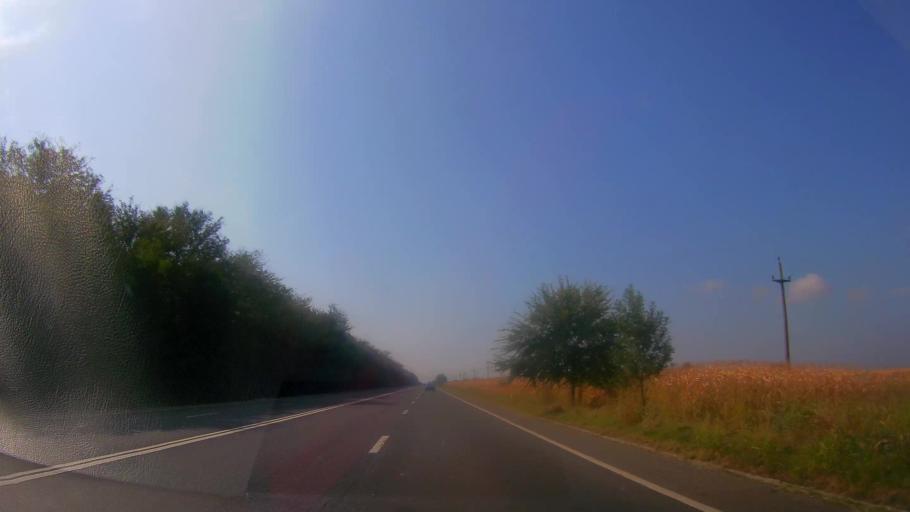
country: RO
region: Giurgiu
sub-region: Comuna Daia
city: Plopsoru
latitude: 44.0448
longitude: 25.9771
